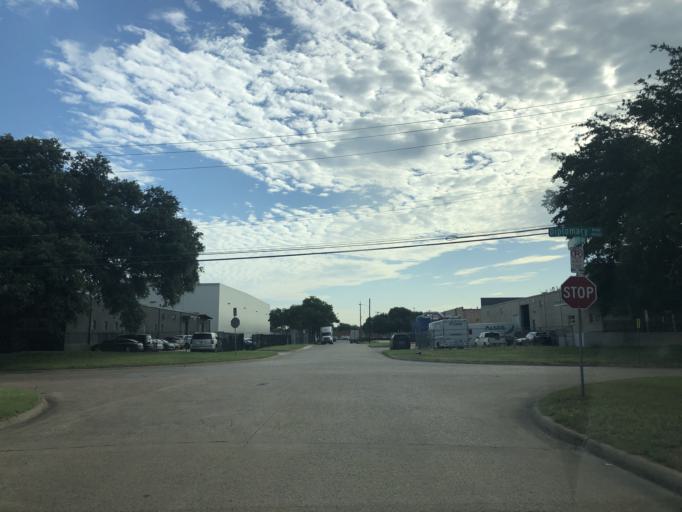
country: US
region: Texas
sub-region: Dallas County
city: Irving
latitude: 32.8176
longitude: -96.8931
